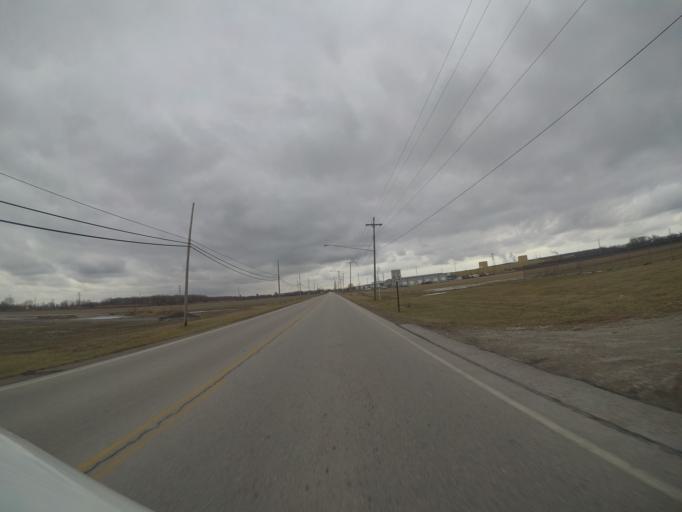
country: US
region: Ohio
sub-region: Wood County
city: Walbridge
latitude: 41.5882
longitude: -83.5126
